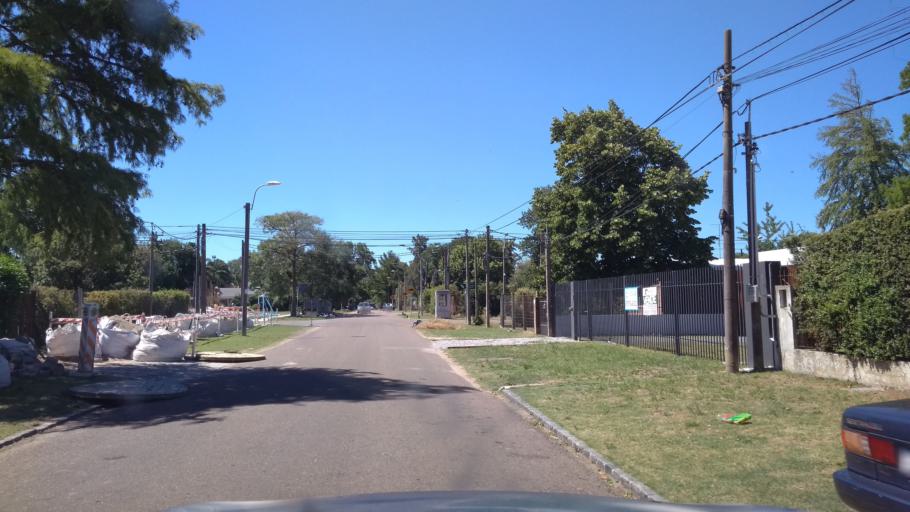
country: UY
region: Canelones
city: Paso de Carrasco
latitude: -34.8713
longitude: -56.0613
